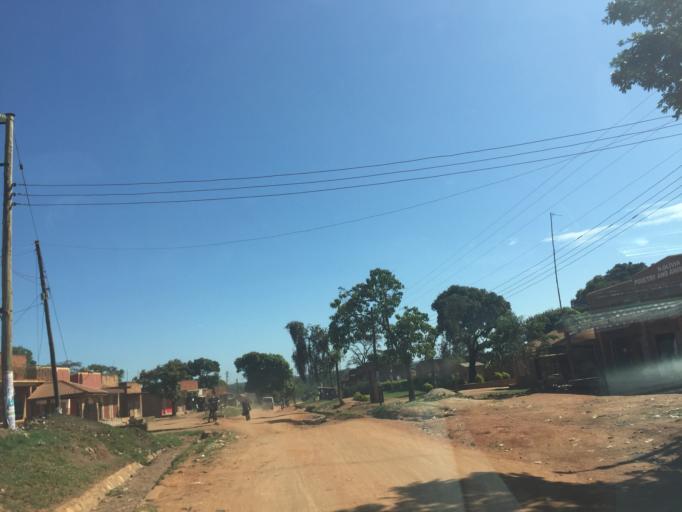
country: UG
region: Central Region
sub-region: Luwero District
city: Luwero
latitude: 0.8359
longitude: 32.5023
